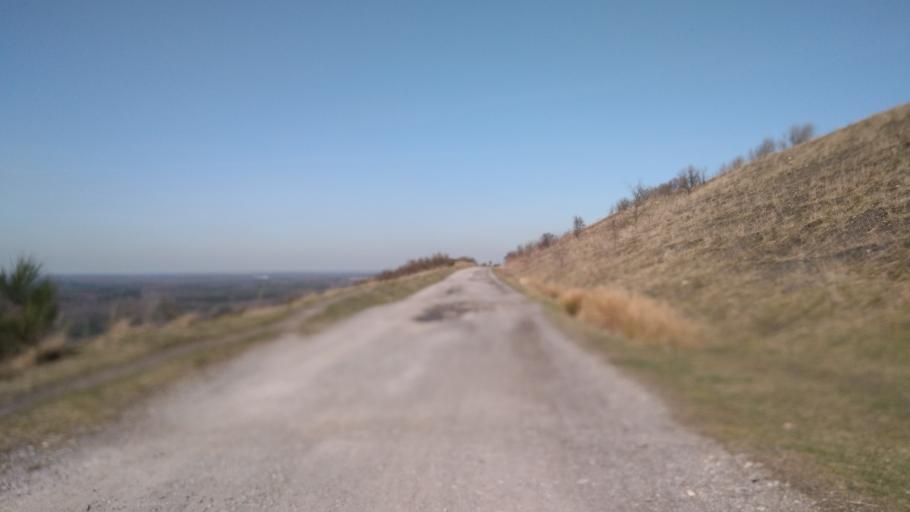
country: DE
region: North Rhine-Westphalia
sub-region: Regierungsbezirk Munster
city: Bottrop
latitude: 51.5512
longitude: 6.8749
